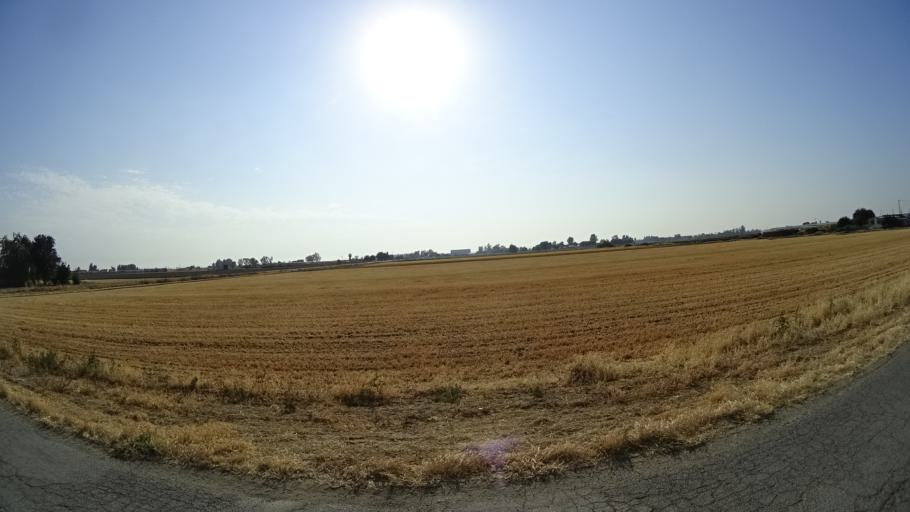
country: US
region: California
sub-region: Fresno County
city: Riverdale
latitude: 36.3796
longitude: -119.8431
